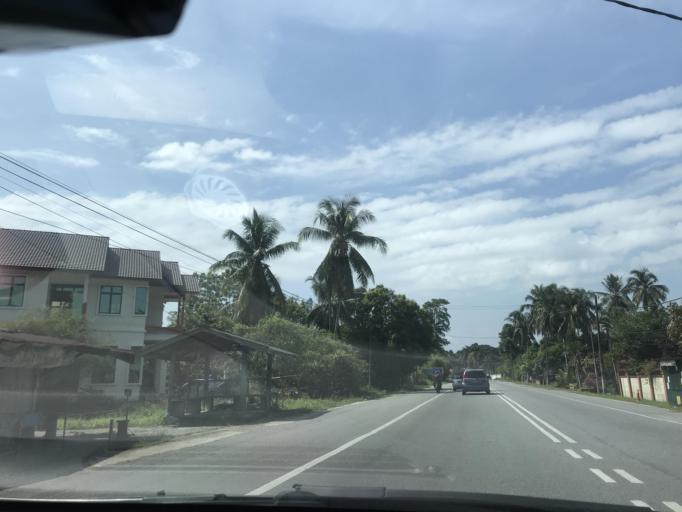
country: MY
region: Kelantan
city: Tumpat
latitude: 6.1348
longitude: 102.1745
